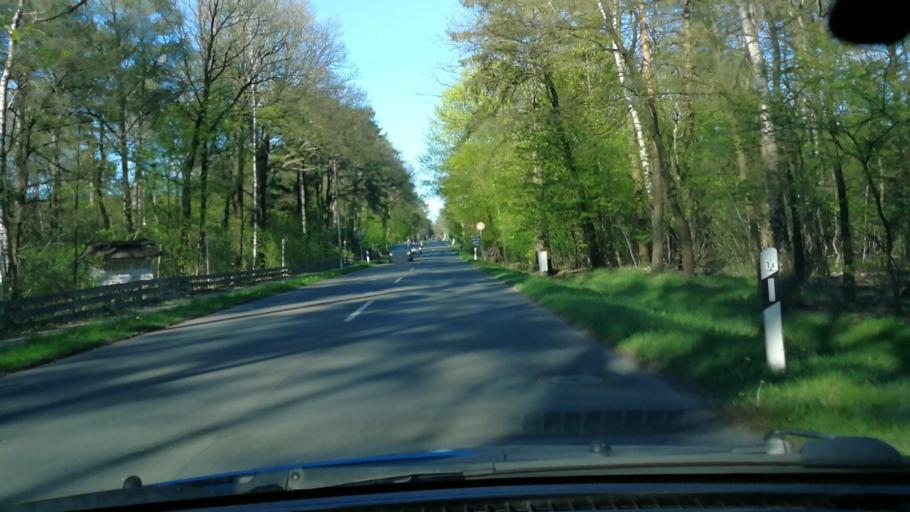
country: DE
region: Lower Saxony
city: Soltau
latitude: 52.9984
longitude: 9.8574
